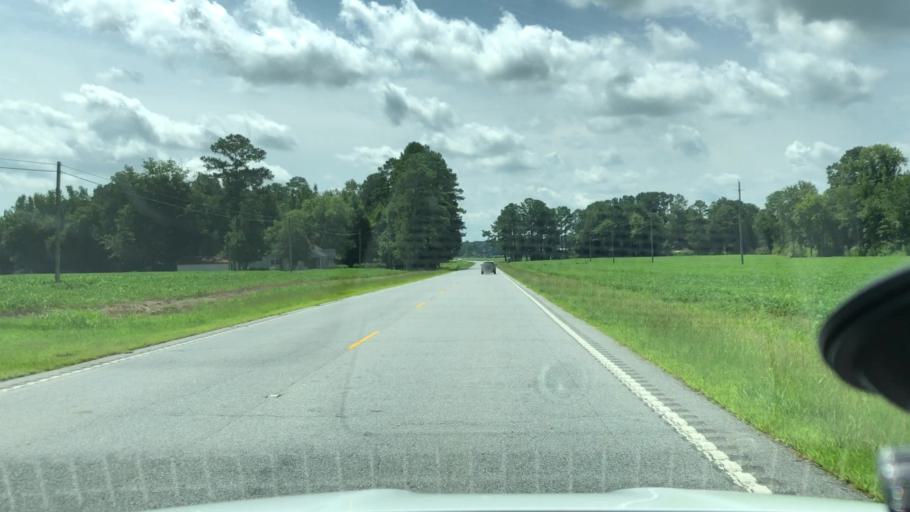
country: US
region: North Carolina
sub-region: Beaufort County
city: Washington
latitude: 35.6581
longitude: -77.0724
